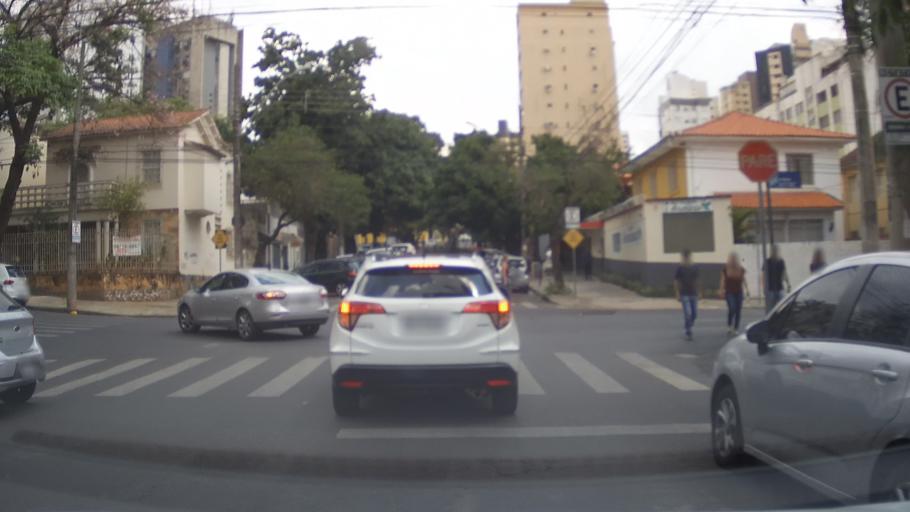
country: BR
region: Minas Gerais
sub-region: Belo Horizonte
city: Belo Horizonte
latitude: -19.9282
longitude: -43.9218
